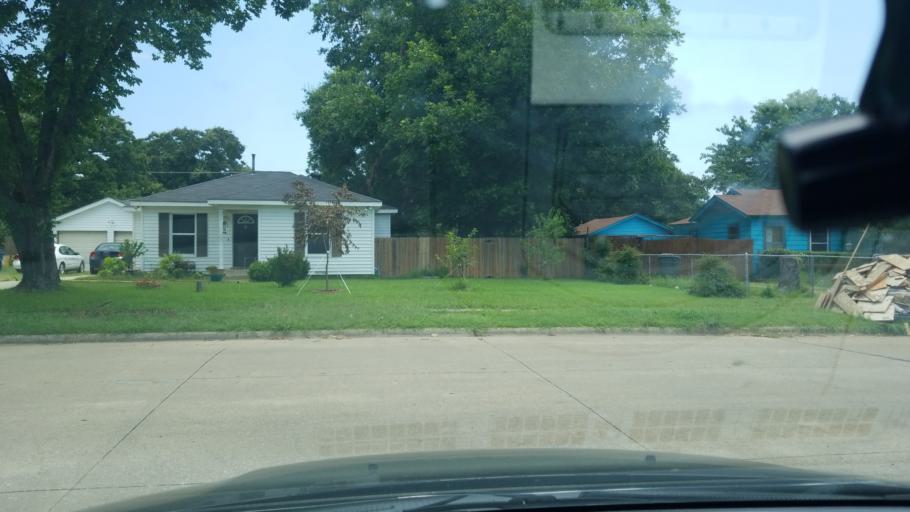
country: US
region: Texas
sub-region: Dallas County
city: Balch Springs
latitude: 32.7186
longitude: -96.6596
